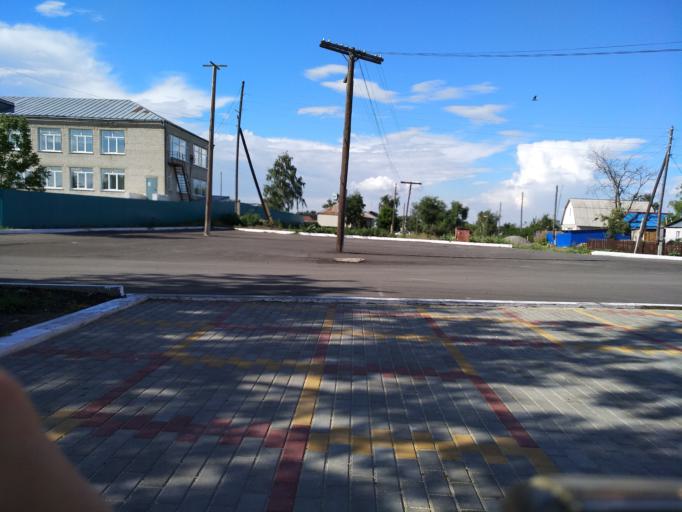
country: RU
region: Lipetsk
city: Dobrinka
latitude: 52.0373
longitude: 40.5547
